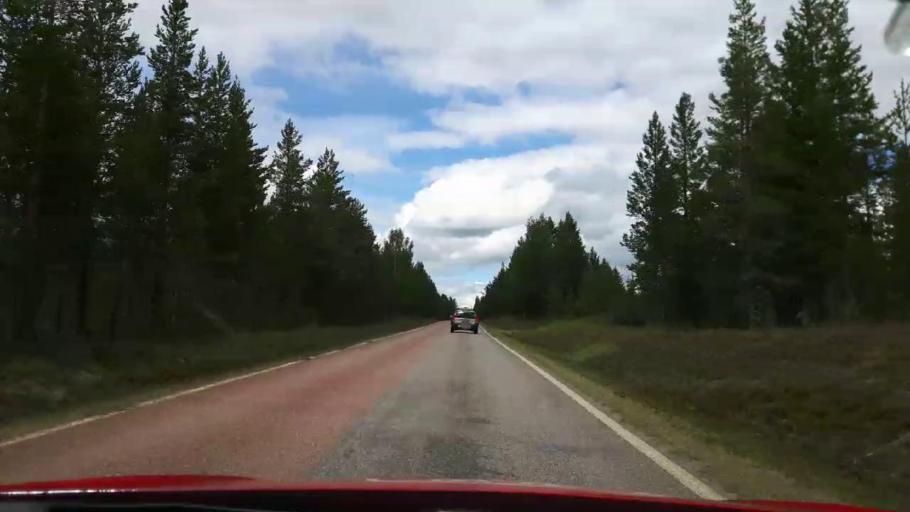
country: NO
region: Hedmark
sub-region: Trysil
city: Innbygda
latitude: 61.8388
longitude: 12.9565
